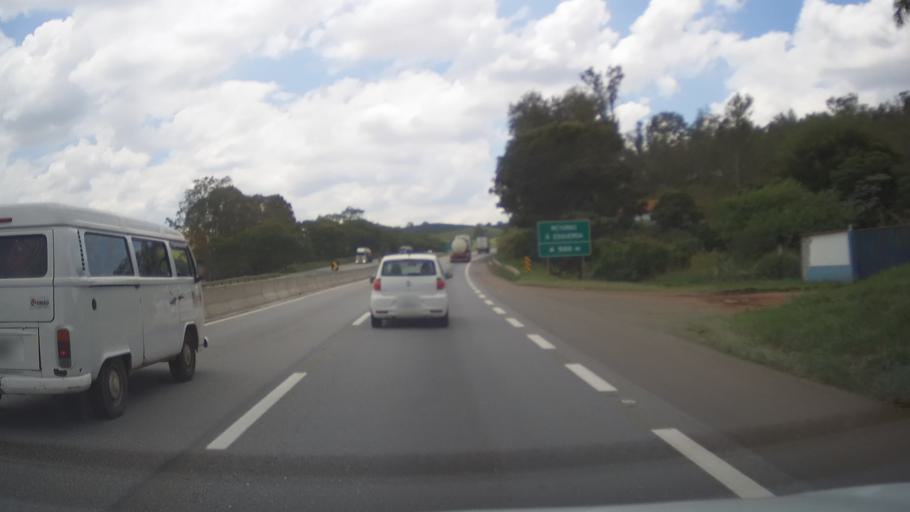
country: BR
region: Minas Gerais
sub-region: Tres Coracoes
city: Tres Coracoes
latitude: -21.7077
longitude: -45.3737
